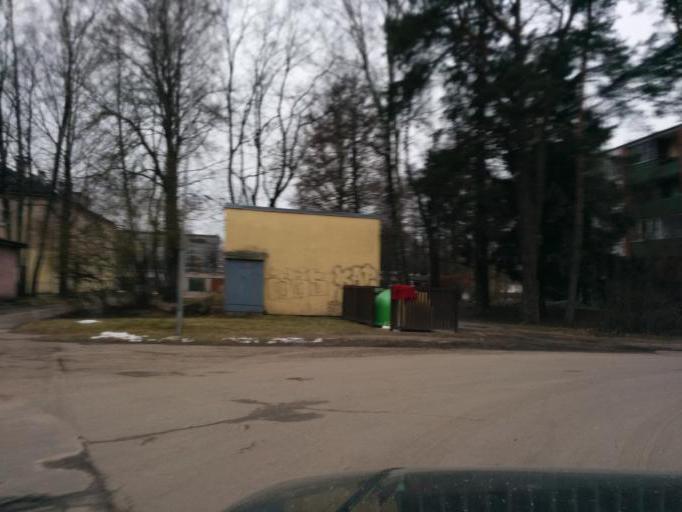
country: LV
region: Jurmala
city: Jurmala
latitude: 56.9649
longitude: 23.8248
